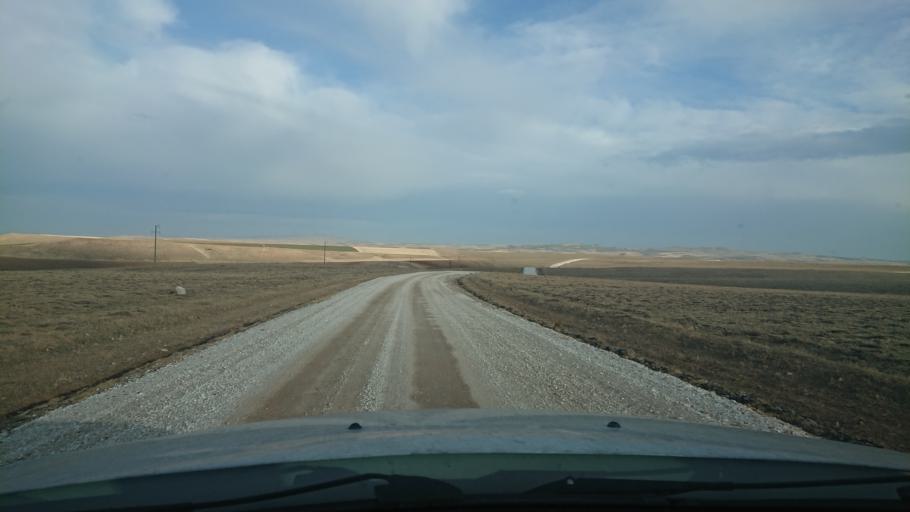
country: TR
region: Aksaray
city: Agacoren
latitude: 38.7325
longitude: 33.8695
